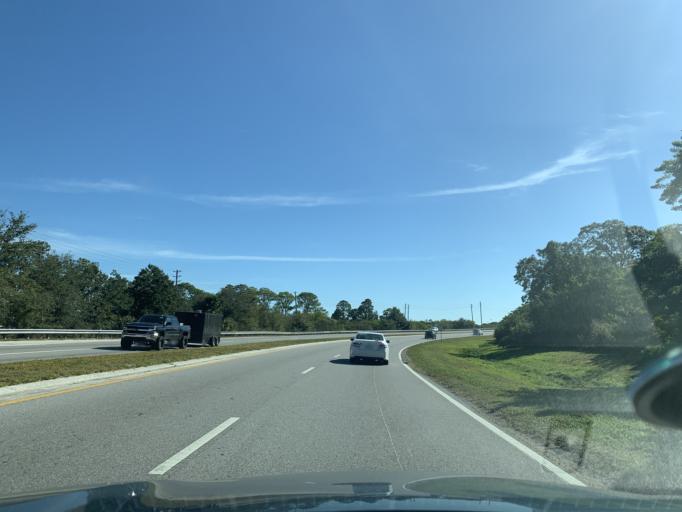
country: US
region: Florida
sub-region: Pinellas County
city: Bay Pines
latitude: 27.8361
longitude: -82.7567
